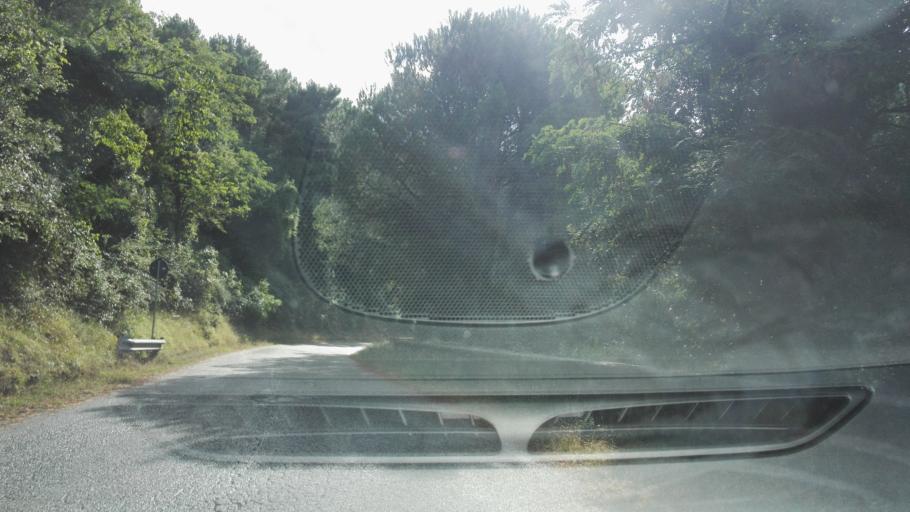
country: IT
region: Calabria
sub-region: Provincia di Reggio Calabria
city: Pazzano
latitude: 38.4636
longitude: 16.4256
